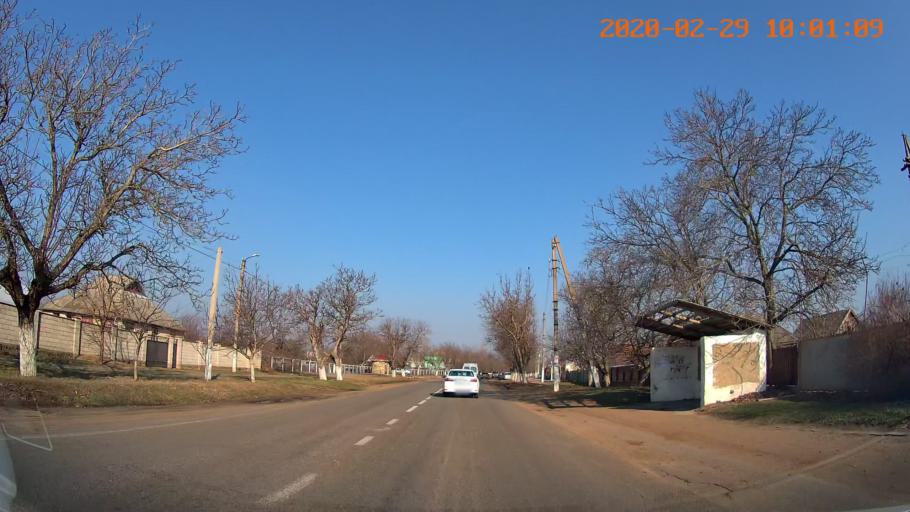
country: MD
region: Telenesti
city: Slobozia
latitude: 46.7733
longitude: 29.6851
